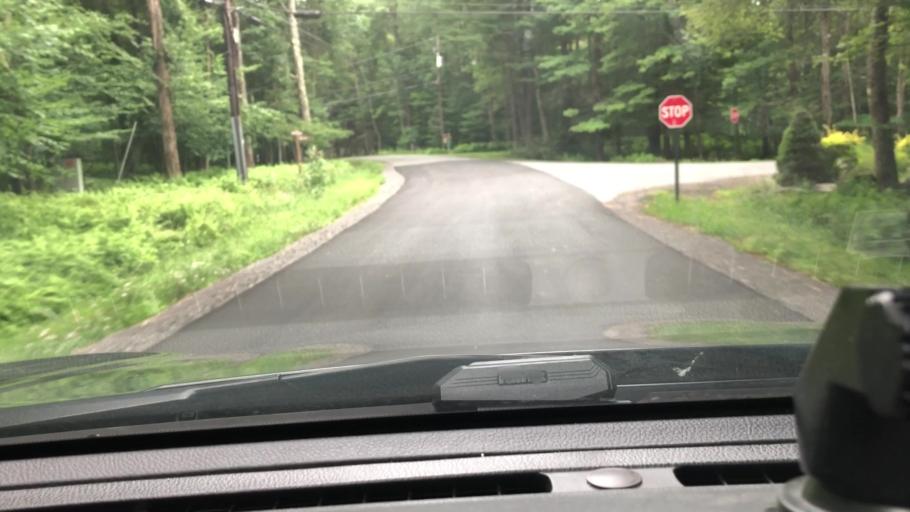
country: US
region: Pennsylvania
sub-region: Lackawanna County
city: Moscow
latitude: 41.2503
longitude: -75.4814
